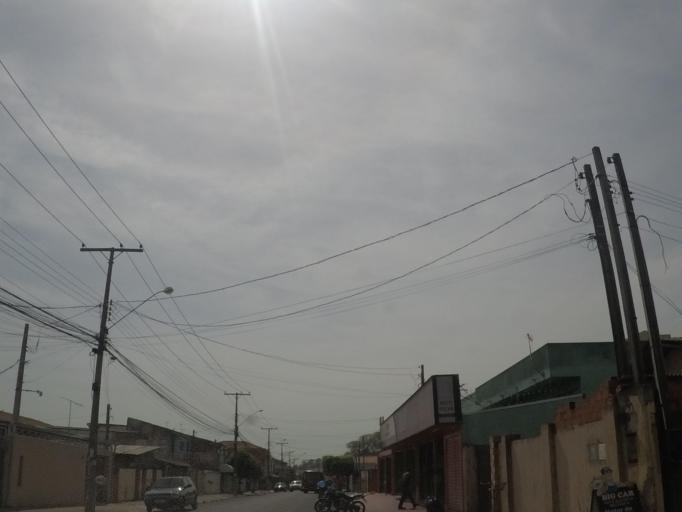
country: BR
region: Sao Paulo
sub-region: Hortolandia
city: Hortolandia
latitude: -22.8518
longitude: -47.1902
